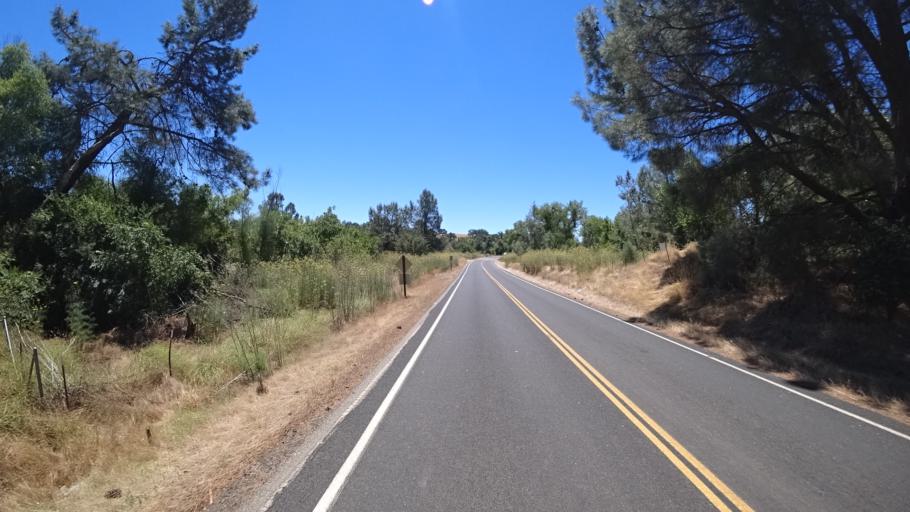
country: US
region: California
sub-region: Calaveras County
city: Rancho Calaveras
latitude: 38.0951
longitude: -120.8721
